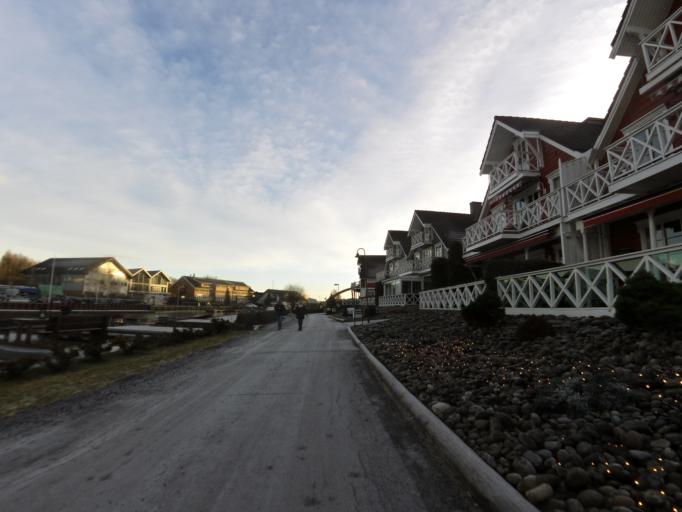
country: NO
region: Ostfold
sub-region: Fredrikstad
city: Fredrikstad
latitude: 59.2242
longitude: 10.9134
